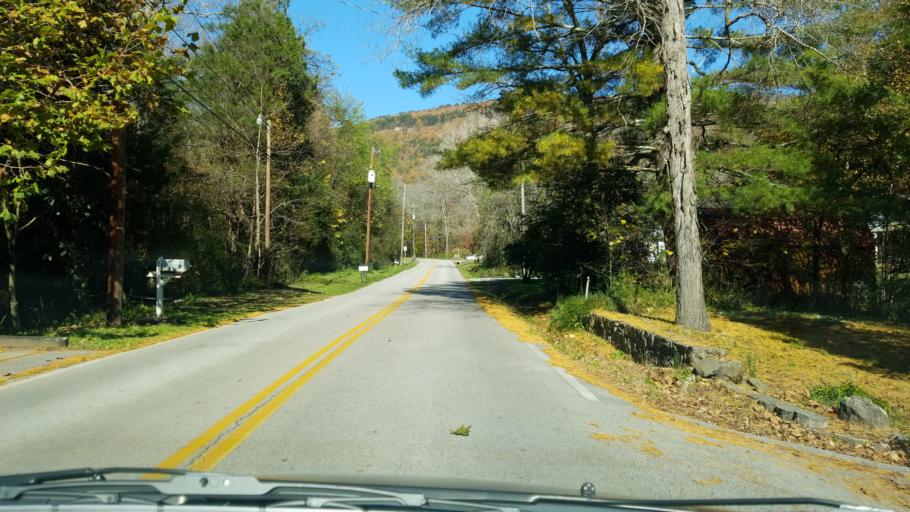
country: US
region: Tennessee
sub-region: Hamilton County
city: Falling Water
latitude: 35.2042
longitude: -85.2545
